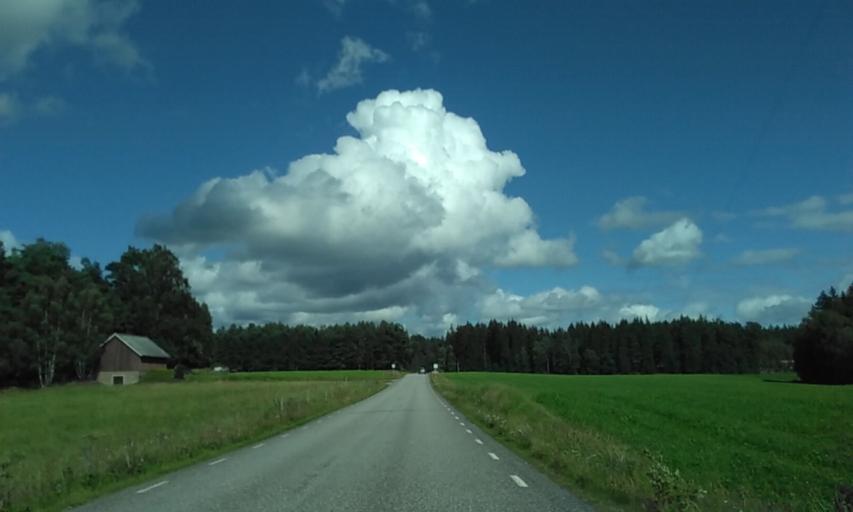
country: SE
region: Vaestra Goetaland
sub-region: Vargarda Kommun
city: Jonstorp
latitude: 57.9406
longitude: 12.7669
